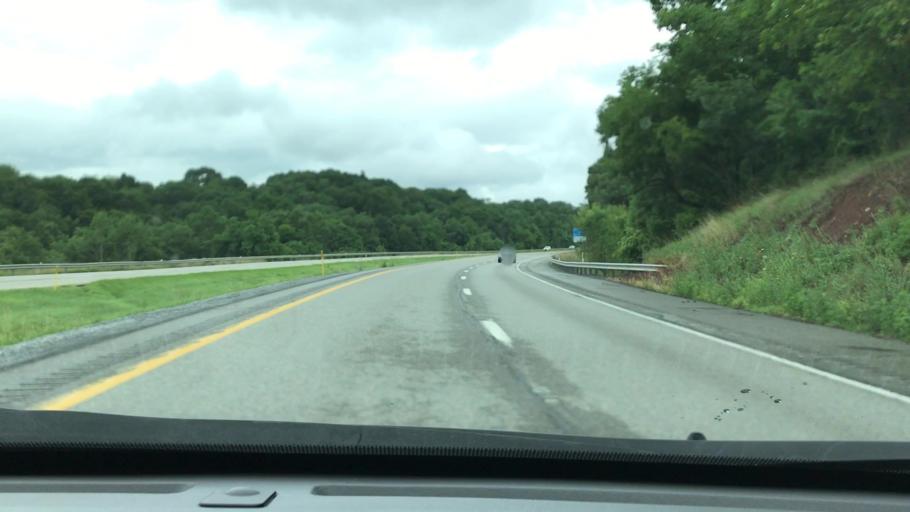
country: US
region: Pennsylvania
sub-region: Bedford County
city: Earlston
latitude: 39.9574
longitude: -78.2458
